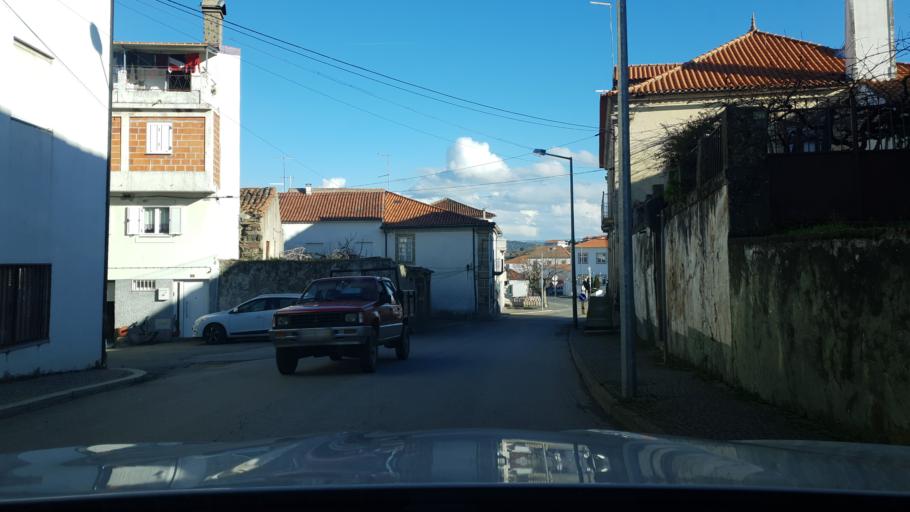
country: PT
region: Braganca
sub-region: Freixo de Espada A Cinta
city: Freixo de Espada a Cinta
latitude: 41.0932
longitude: -6.8104
